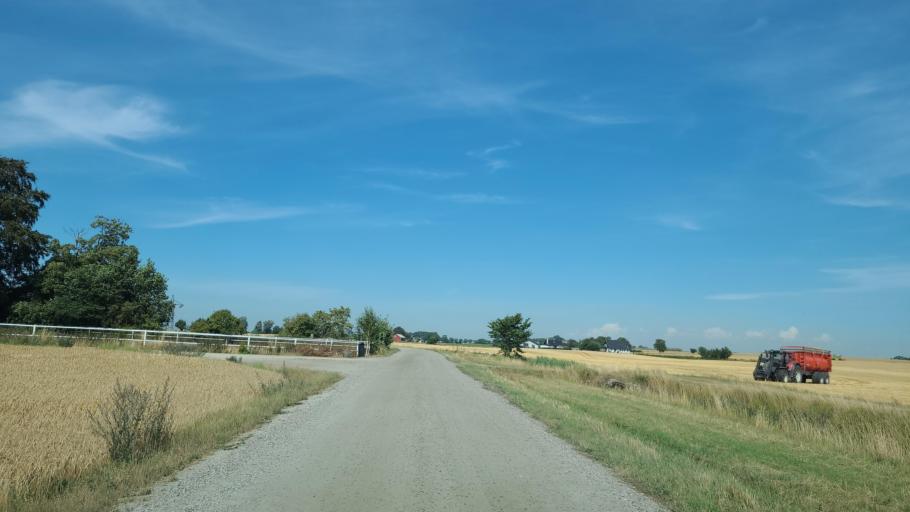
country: SE
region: Skane
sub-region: Trelleborgs Kommun
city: Skare
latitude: 55.4202
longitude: 13.0654
